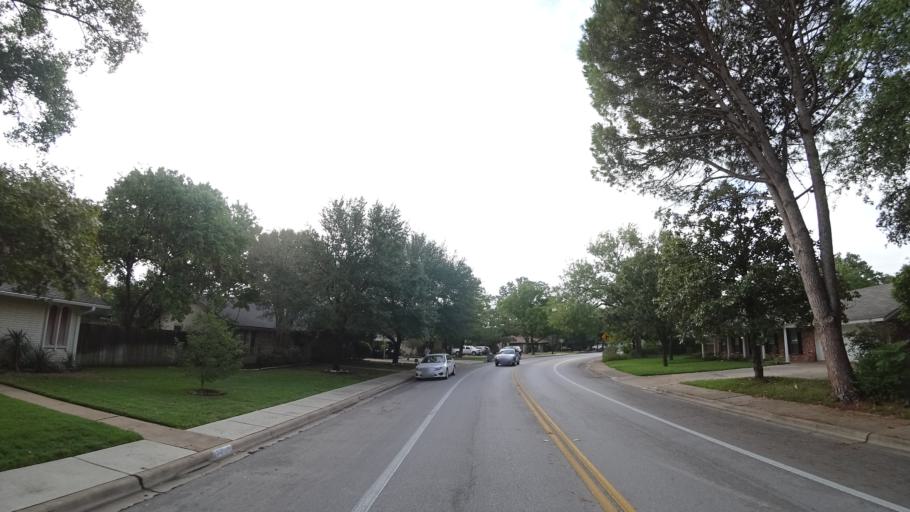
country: US
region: Texas
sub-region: Travis County
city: West Lake Hills
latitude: 30.3574
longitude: -97.7402
